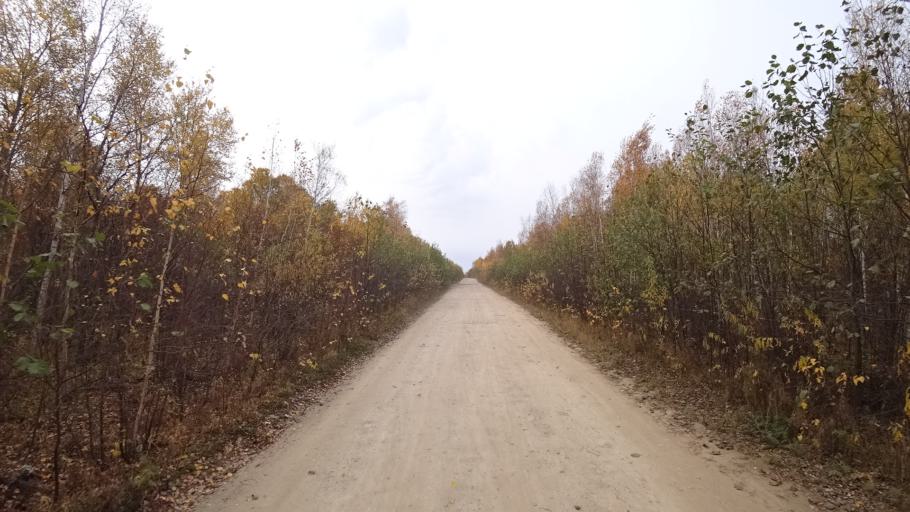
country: RU
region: Khabarovsk Krai
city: Amursk
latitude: 50.1450
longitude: 136.9687
